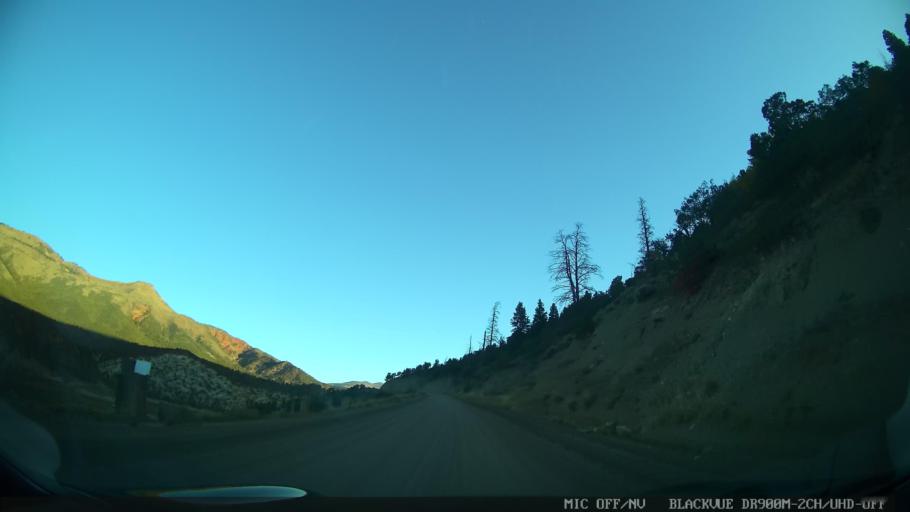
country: US
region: Colorado
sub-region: Eagle County
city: Edwards
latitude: 39.8952
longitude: -106.6068
